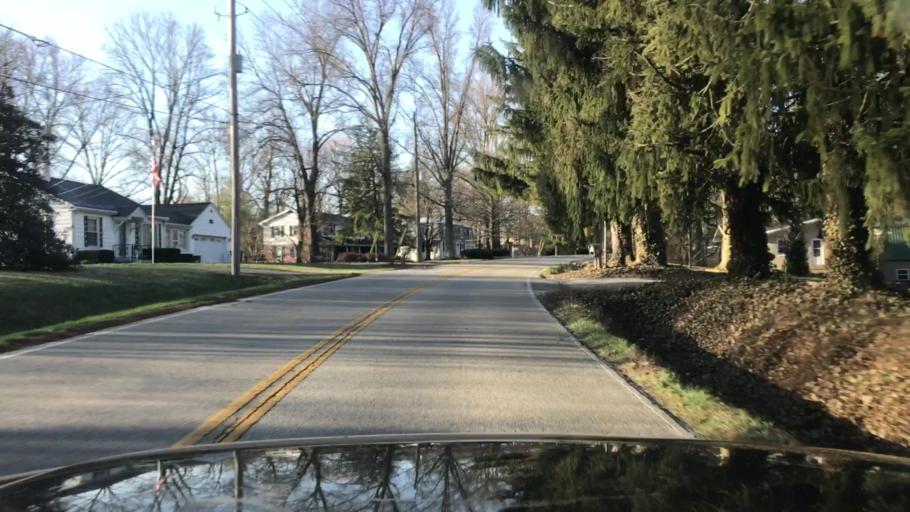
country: US
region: Indiana
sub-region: Vanderburgh County
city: Highland
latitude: 38.0384
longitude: -87.5622
